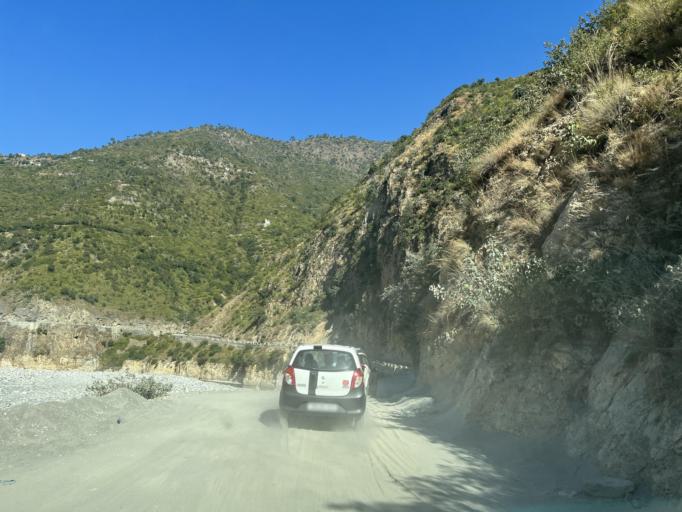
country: IN
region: Uttarakhand
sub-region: Naini Tal
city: Naini Tal
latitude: 29.5066
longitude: 79.4532
